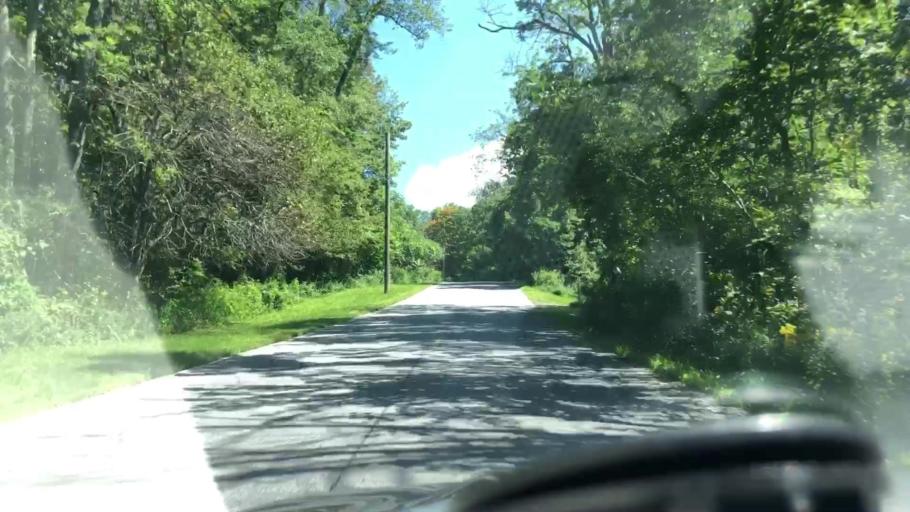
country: US
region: Massachusetts
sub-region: Berkshire County
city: Lanesborough
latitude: 42.5485
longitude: -73.2166
